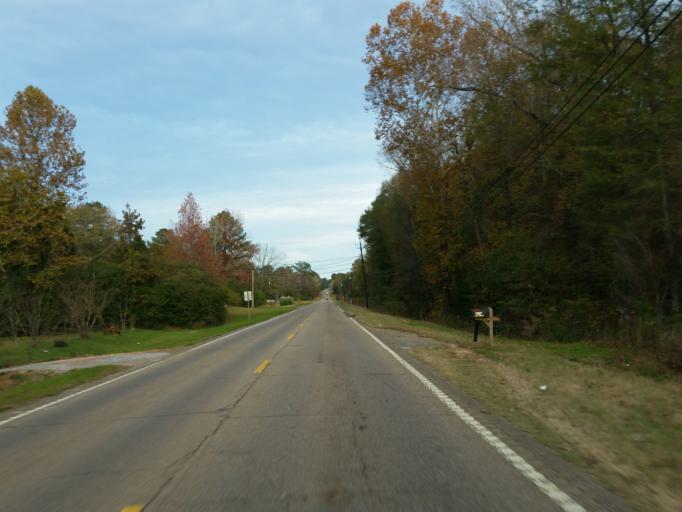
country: US
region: Mississippi
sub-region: Lauderdale County
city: Marion
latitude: 32.4055
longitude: -88.5890
